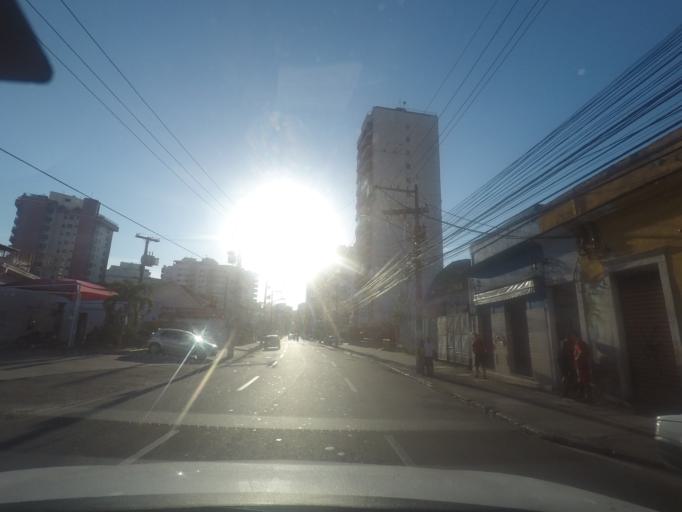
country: BR
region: Rio de Janeiro
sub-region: Niteroi
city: Niteroi
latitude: -22.8986
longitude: -43.1052
